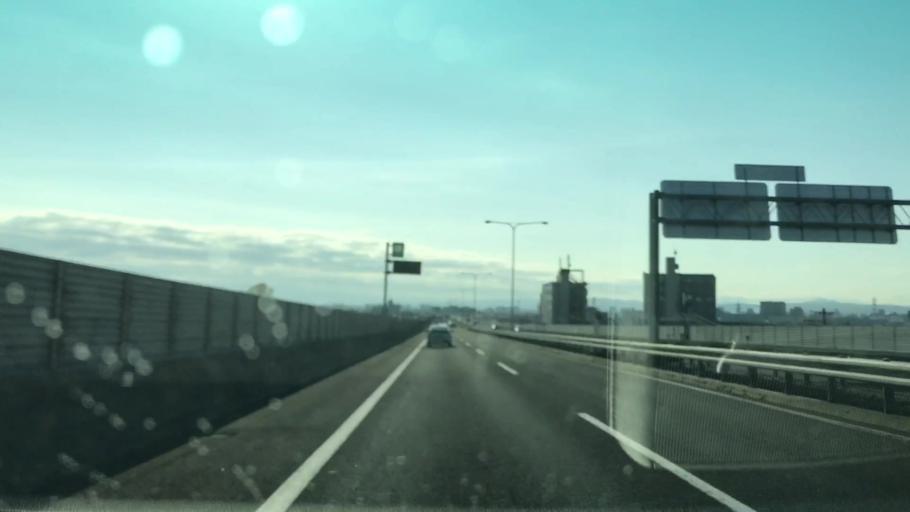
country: JP
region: Hokkaido
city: Sapporo
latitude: 43.0696
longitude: 141.4226
